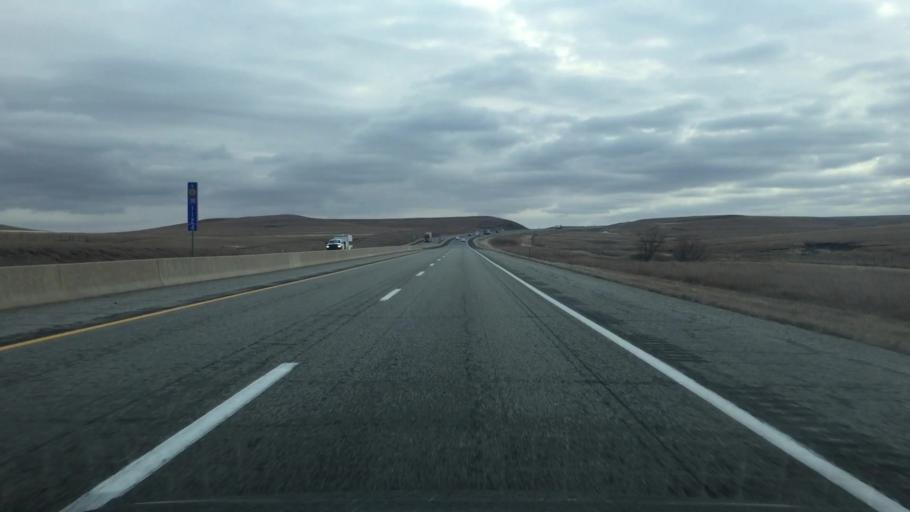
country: US
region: Kansas
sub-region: Chase County
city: Cottonwood Falls
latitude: 38.2475
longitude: -96.3938
